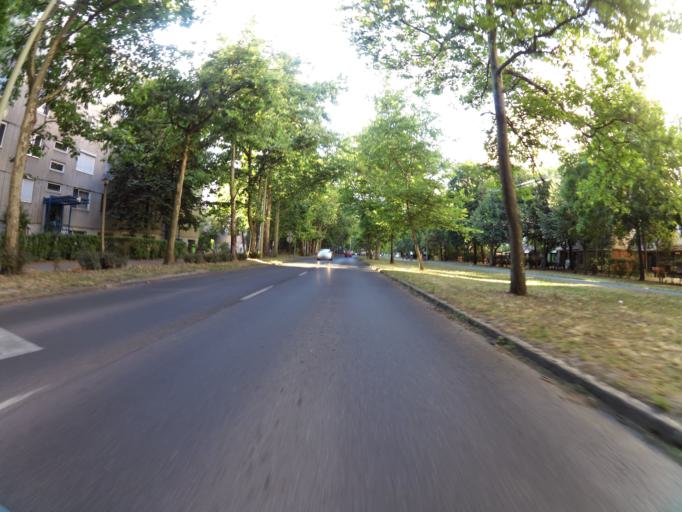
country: HU
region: Csongrad
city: Szeged
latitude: 46.2644
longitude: 20.1690
